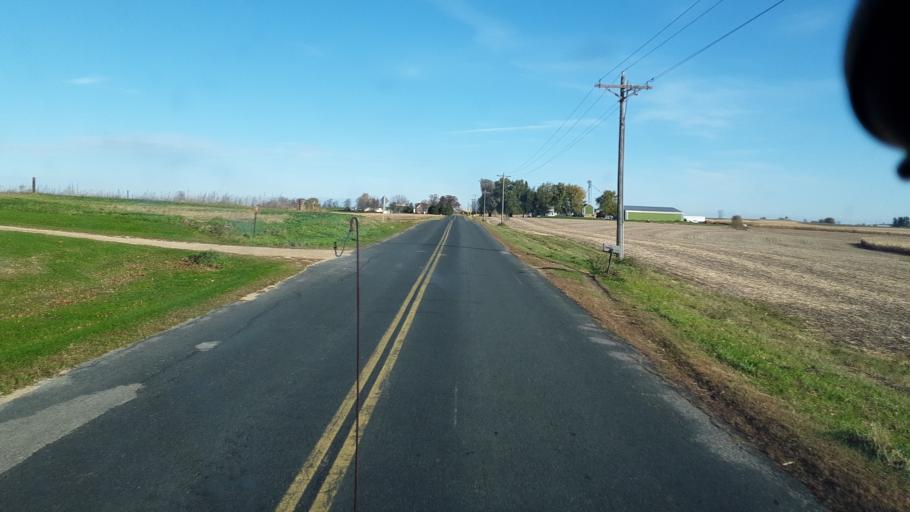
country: US
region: Wisconsin
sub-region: Vernon County
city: Hillsboro
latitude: 43.7350
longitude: -90.4427
